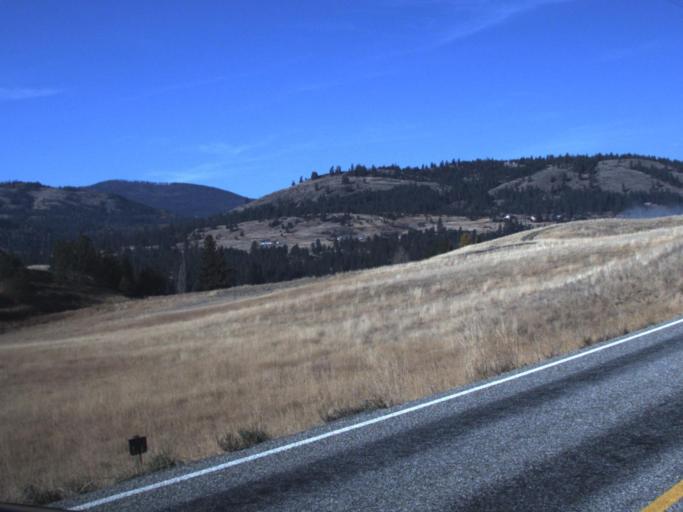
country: US
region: Washington
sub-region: Ferry County
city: Republic
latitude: 48.7333
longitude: -118.6570
